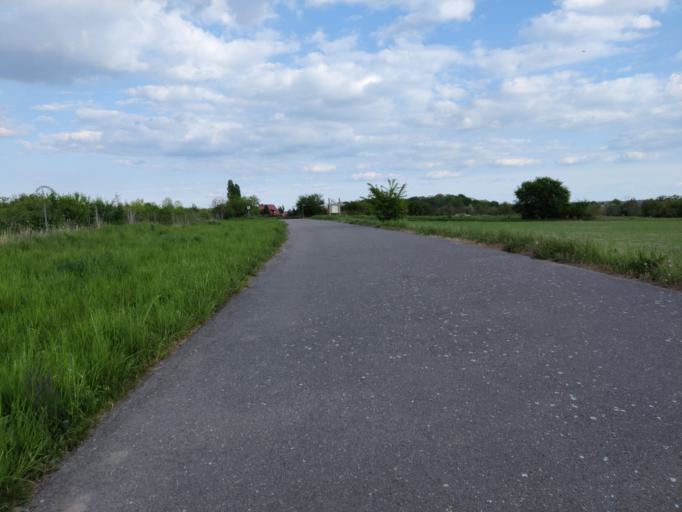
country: DE
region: Saxony
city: Espenhain
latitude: 51.2232
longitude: 12.4588
